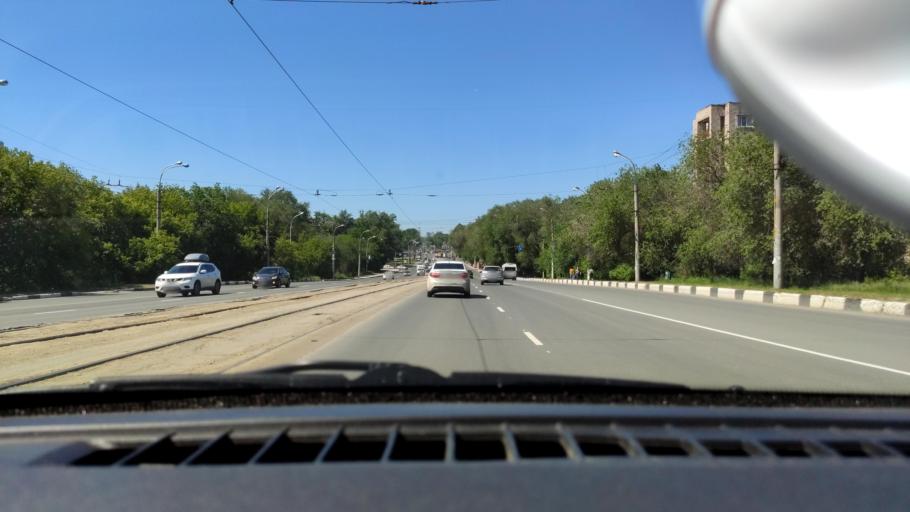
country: RU
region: Samara
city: Samara
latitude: 53.2144
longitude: 50.2699
